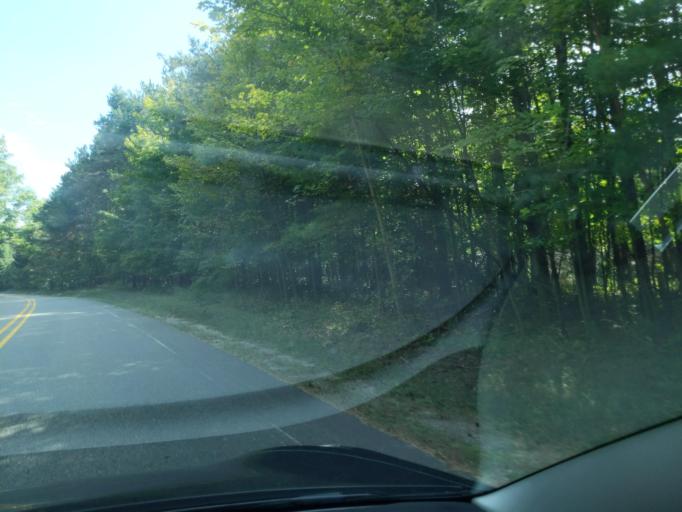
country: US
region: Michigan
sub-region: Antrim County
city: Bellaire
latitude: 45.0544
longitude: -85.3182
